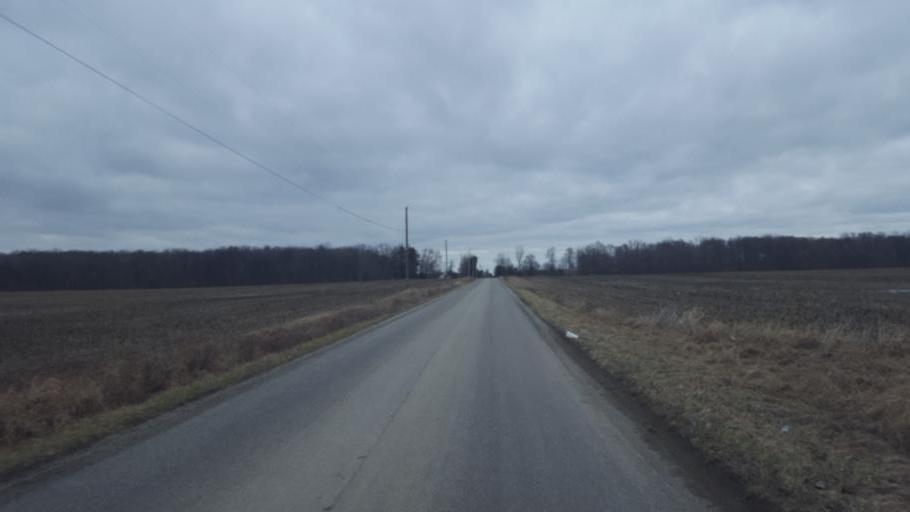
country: US
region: Ohio
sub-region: Crawford County
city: Galion
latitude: 40.6425
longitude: -82.7848
